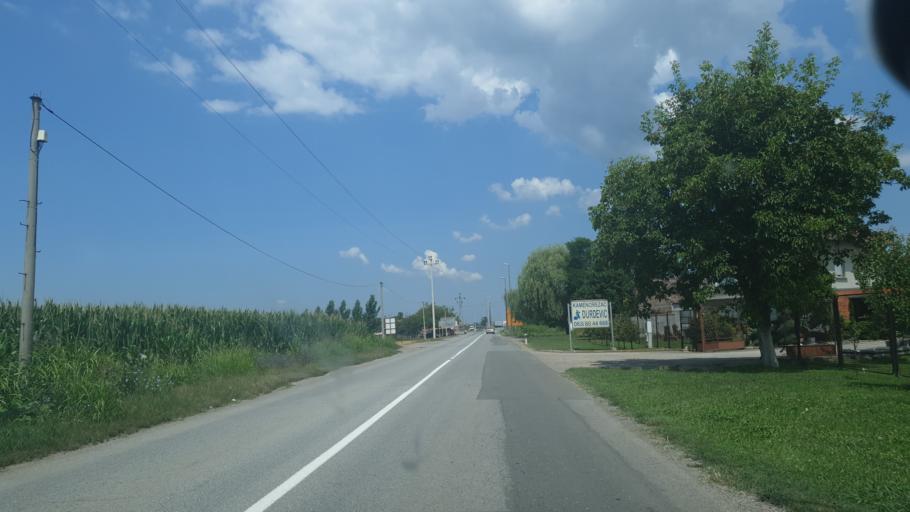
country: RS
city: Ravnje
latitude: 45.0319
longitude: 19.3888
